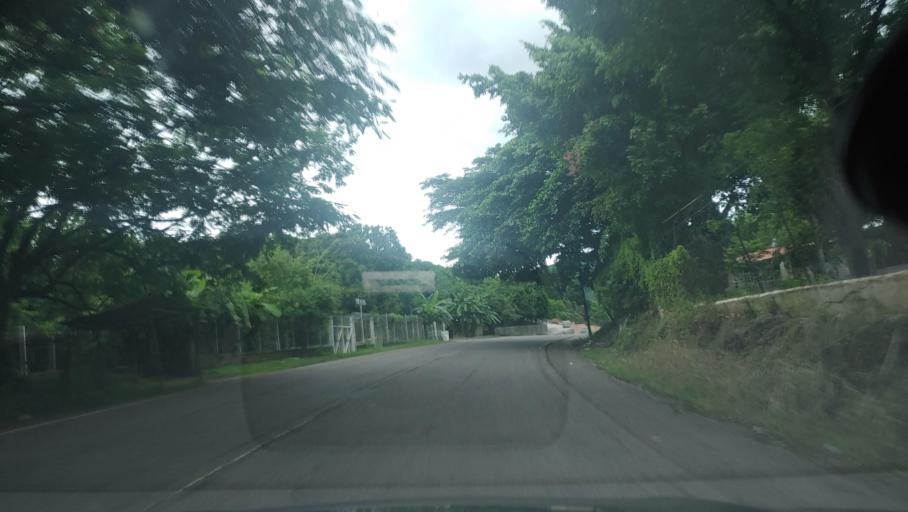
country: HN
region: Choluteca
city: Corpus
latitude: 13.3710
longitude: -87.0348
